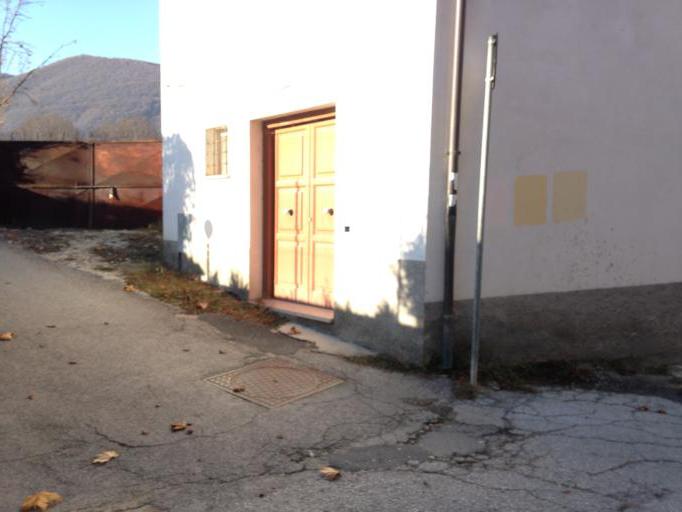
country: IT
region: Umbria
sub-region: Provincia di Perugia
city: Norcia
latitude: 42.7940
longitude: 13.0901
